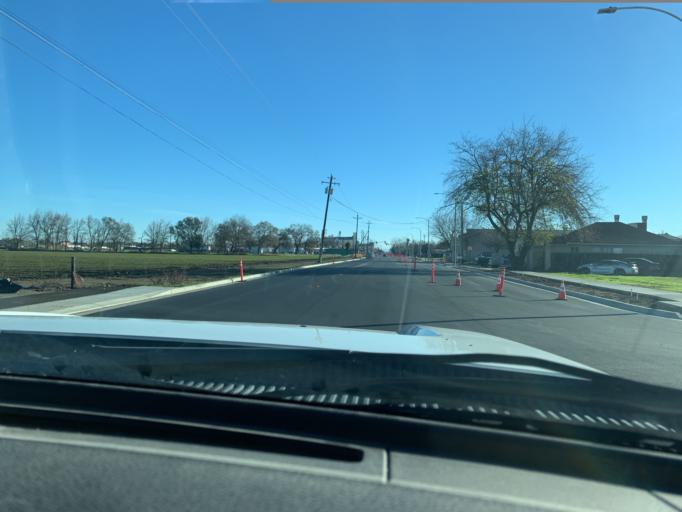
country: US
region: California
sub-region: Yolo County
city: Woodland
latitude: 38.6919
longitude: -121.7782
